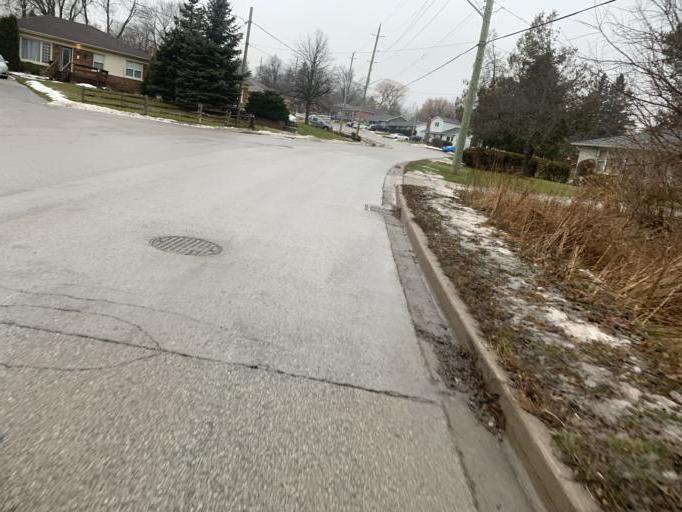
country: CA
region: Ontario
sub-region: Halton
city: Milton
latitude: 43.6564
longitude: -79.9273
